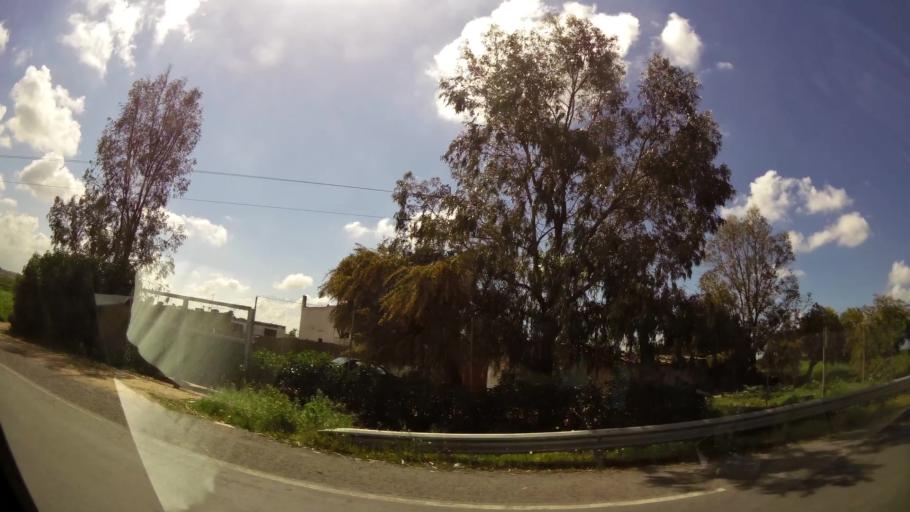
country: MA
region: Grand Casablanca
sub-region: Nouaceur
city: Bouskoura
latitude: 33.5017
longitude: -7.6082
